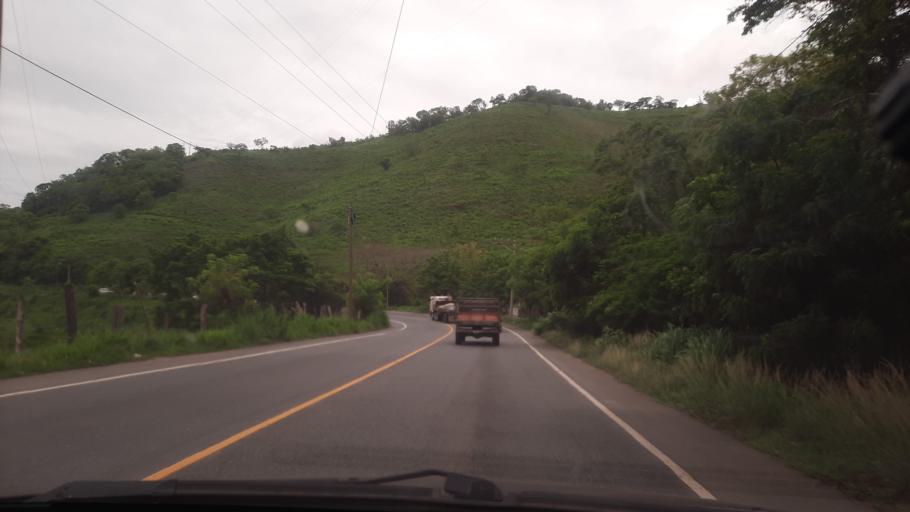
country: GT
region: Zacapa
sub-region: Municipio de Zacapa
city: Gualan
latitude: 15.1625
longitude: -89.3142
